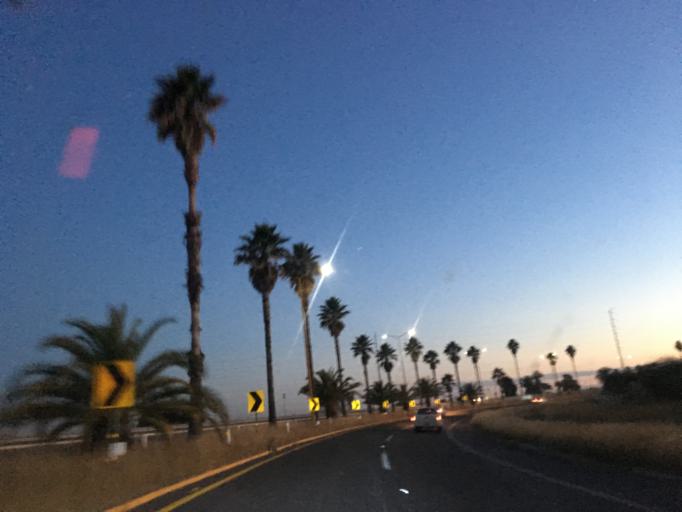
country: MX
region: Aguascalientes
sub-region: Aguascalientes
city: Penuelas (El Cienegal)
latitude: 21.7239
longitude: -102.3099
